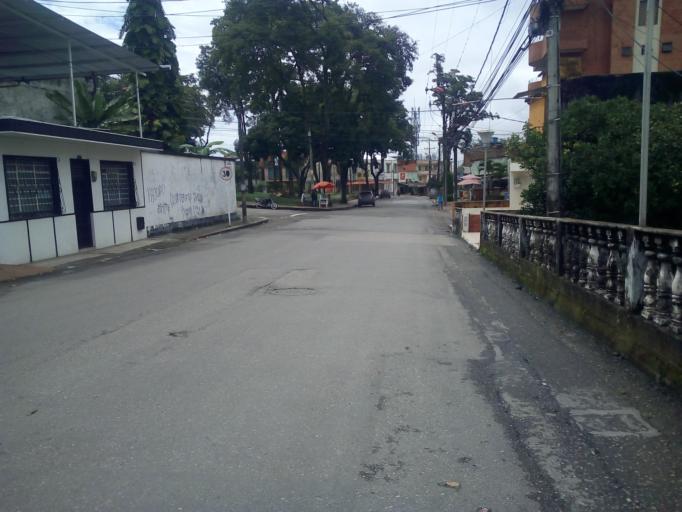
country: CO
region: Tolima
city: Ibague
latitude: 4.4510
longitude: -75.2448
